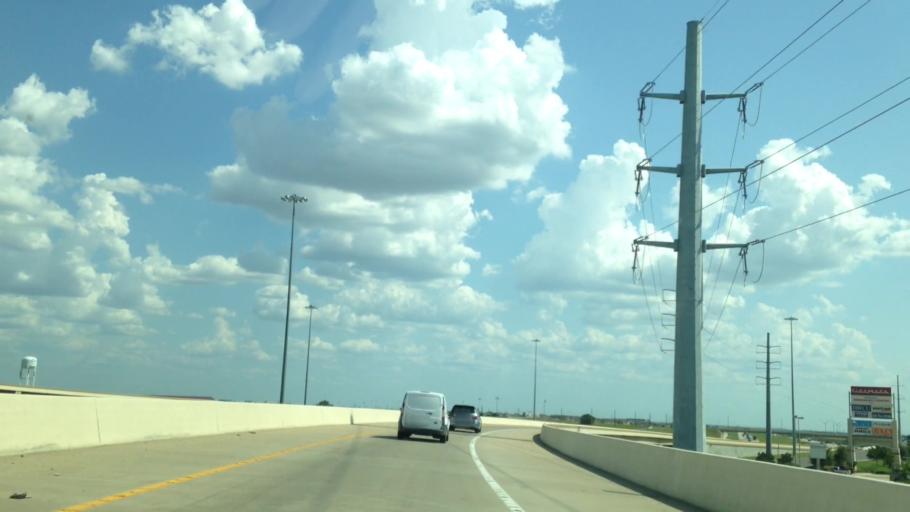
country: US
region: Texas
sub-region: Travis County
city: Pflugerville
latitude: 30.4730
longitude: -97.5941
